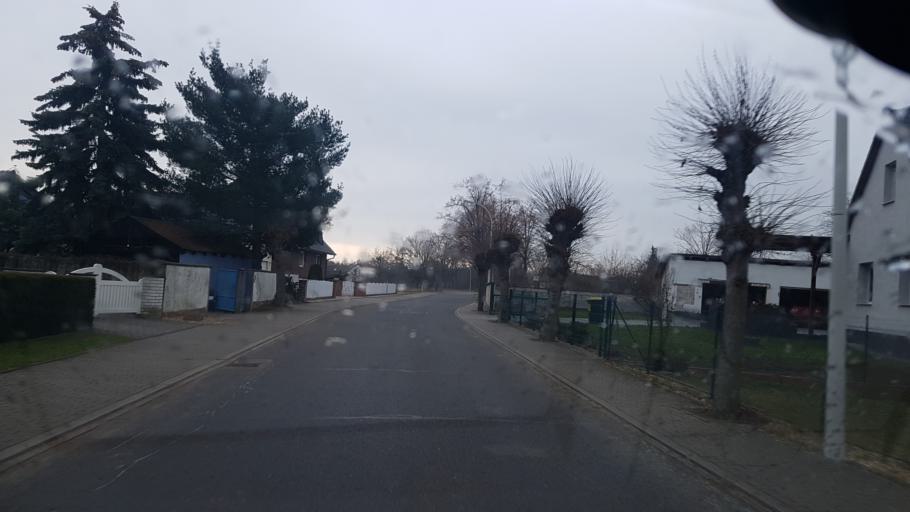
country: DE
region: Brandenburg
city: Cottbus
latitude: 51.7601
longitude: 14.4120
